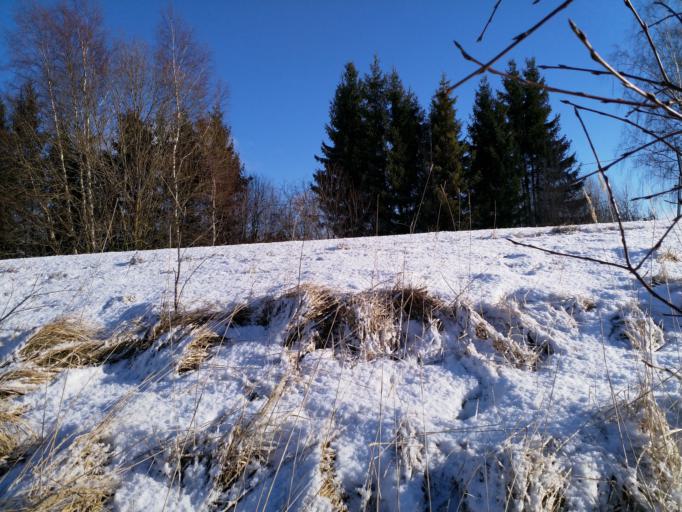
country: LV
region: Aizpute
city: Aizpute
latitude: 56.6595
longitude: 21.6435
